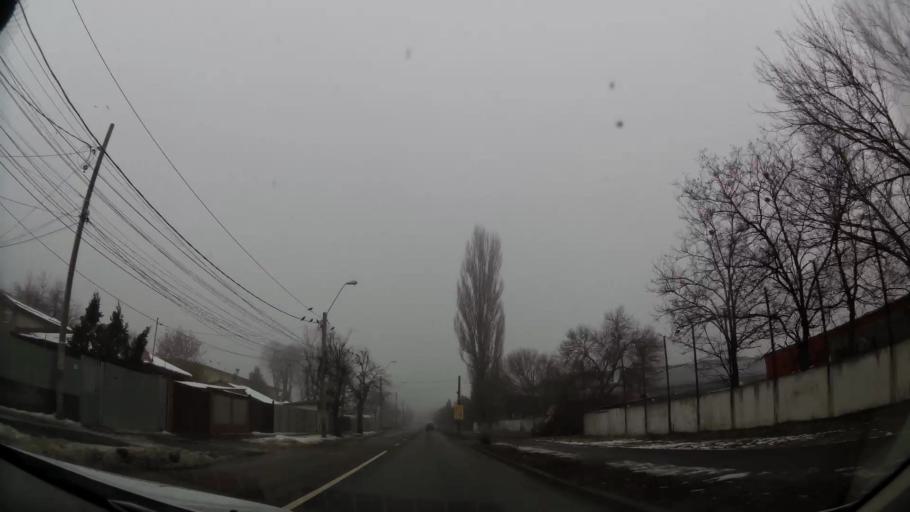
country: RO
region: Ilfov
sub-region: Comuna Chiajna
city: Rosu
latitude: 44.4718
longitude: 26.0194
